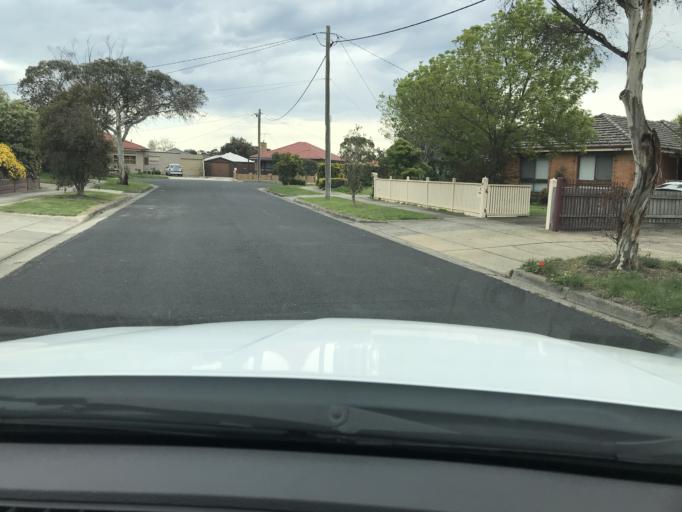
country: AU
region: Victoria
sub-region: Hume
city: Craigieburn
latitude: -37.5966
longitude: 144.9403
